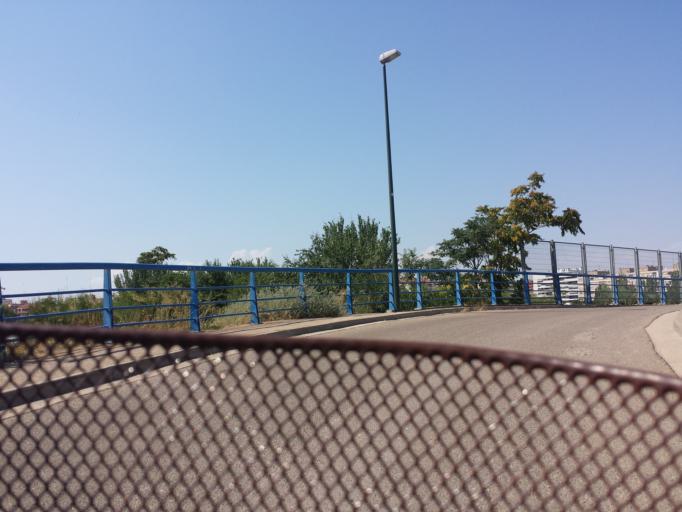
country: ES
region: Aragon
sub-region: Provincia de Zaragoza
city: Zaragoza
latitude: 41.6337
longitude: -0.8702
